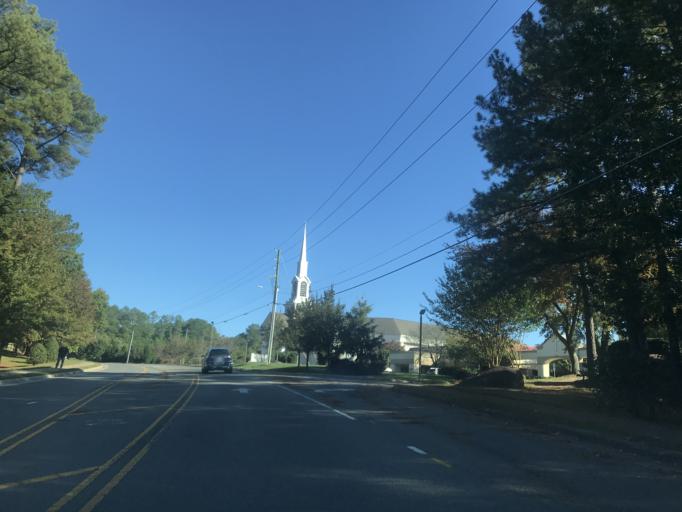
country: US
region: North Carolina
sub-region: Wake County
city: West Raleigh
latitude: 35.8785
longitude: -78.6429
